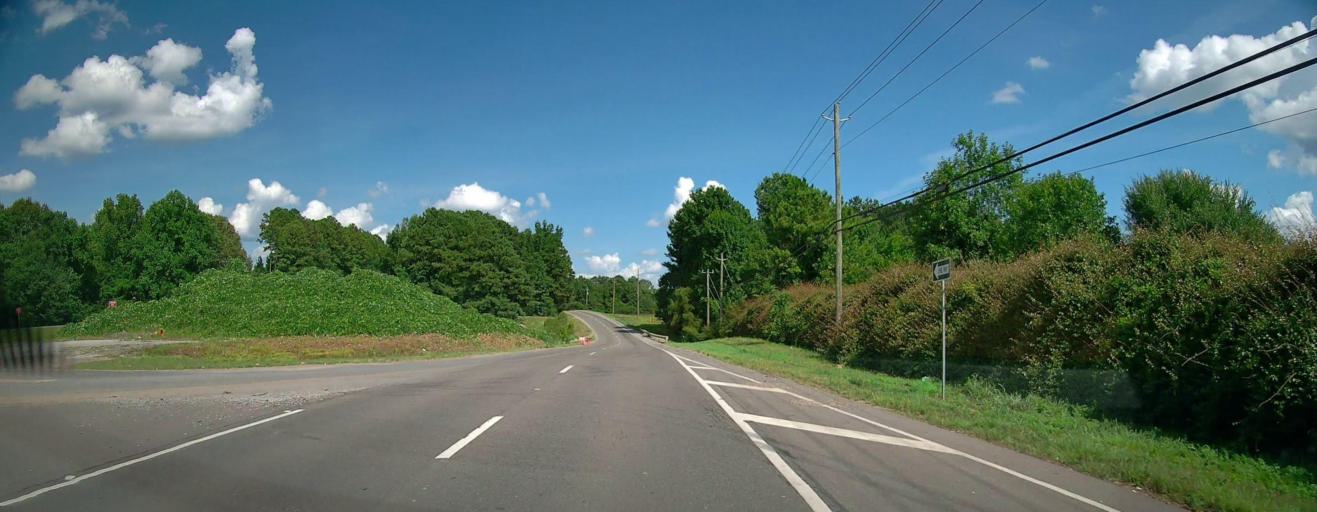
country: US
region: Alabama
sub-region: Tuscaloosa County
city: Northport
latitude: 33.2376
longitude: -87.6560
